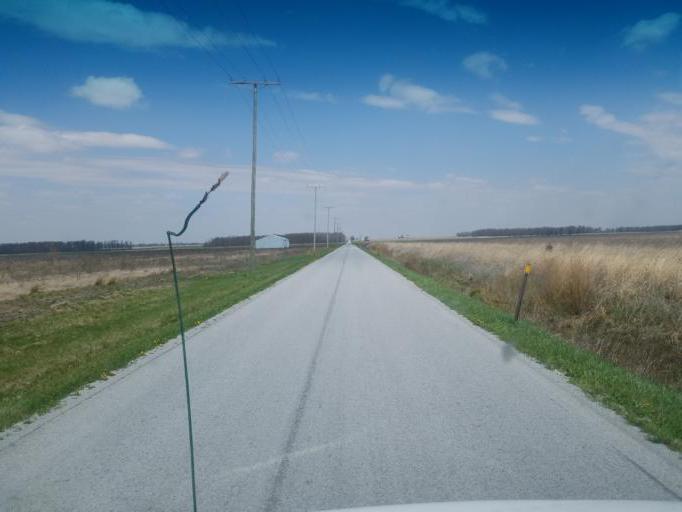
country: US
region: Ohio
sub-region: Hardin County
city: Forest
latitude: 40.7662
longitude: -83.4966
